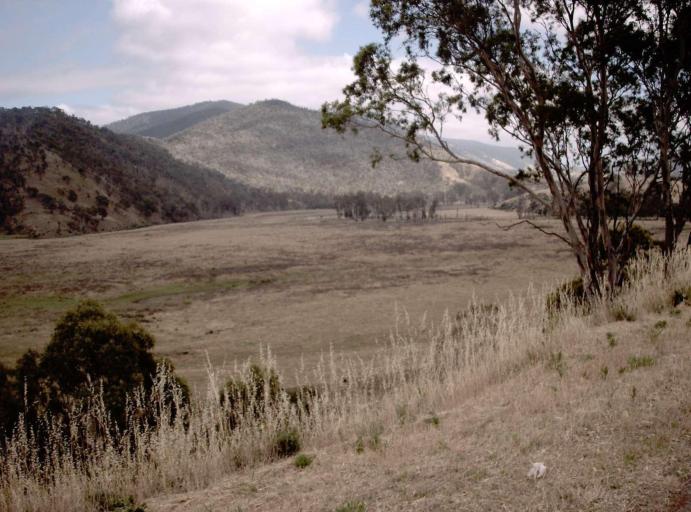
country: AU
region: Victoria
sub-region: Wellington
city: Heyfield
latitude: -37.6660
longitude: 146.6459
